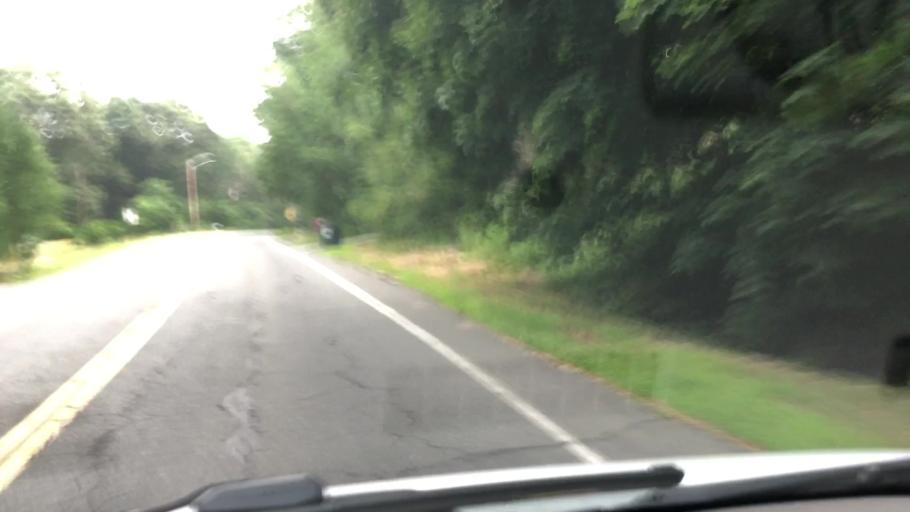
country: US
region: Massachusetts
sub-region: Hampshire County
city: Easthampton
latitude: 42.3025
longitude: -72.6744
